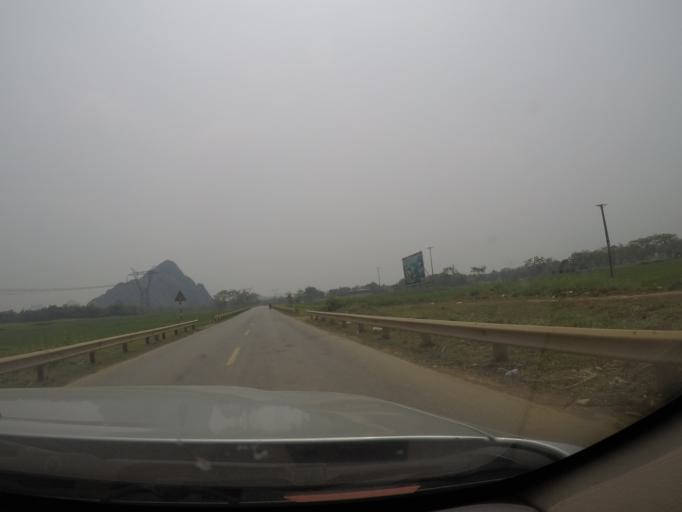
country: VN
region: Thanh Hoa
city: Thi Tran Thuong Xuan
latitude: 19.9246
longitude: 105.3942
